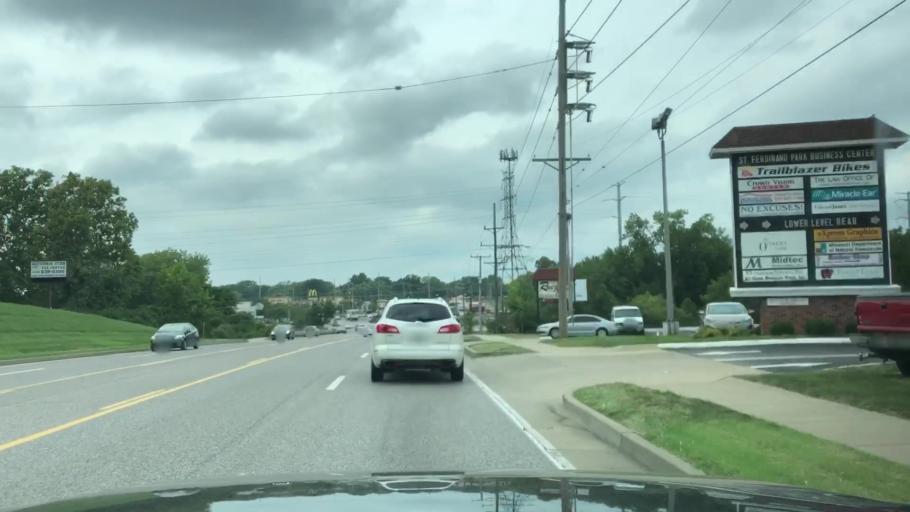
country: US
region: Missouri
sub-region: Saint Louis County
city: Florissant
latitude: 38.7997
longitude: -90.3302
